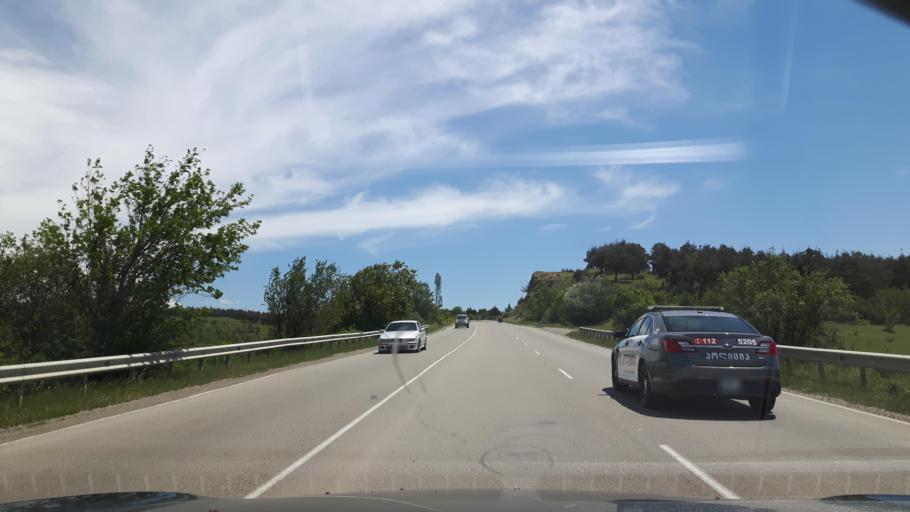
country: GE
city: Didi Lilo
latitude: 41.6925
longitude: 45.0729
